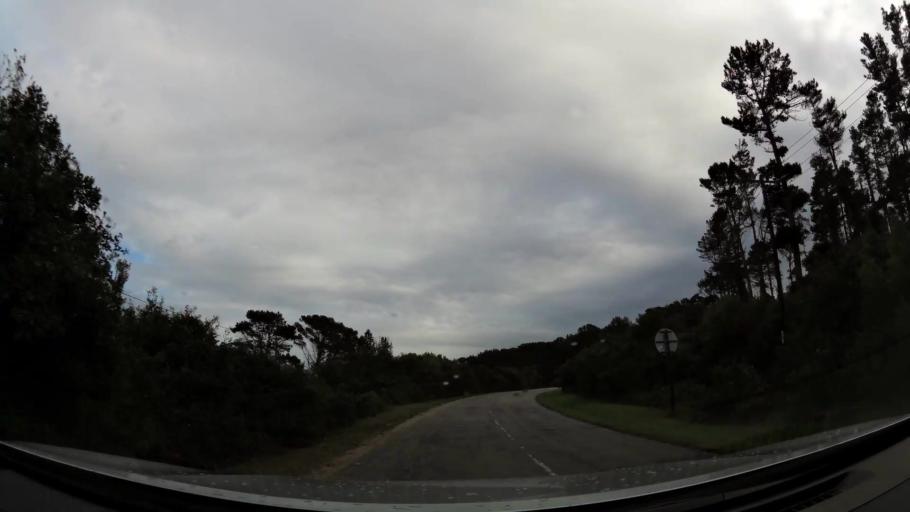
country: ZA
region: Eastern Cape
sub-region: Nelson Mandela Bay Metropolitan Municipality
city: Port Elizabeth
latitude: -34.0090
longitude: 25.4915
